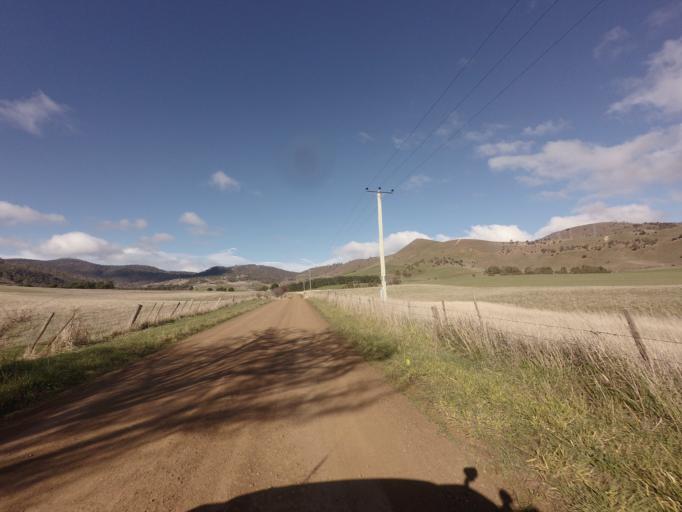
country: AU
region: Tasmania
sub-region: Derwent Valley
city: New Norfolk
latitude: -42.6963
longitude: 146.9722
